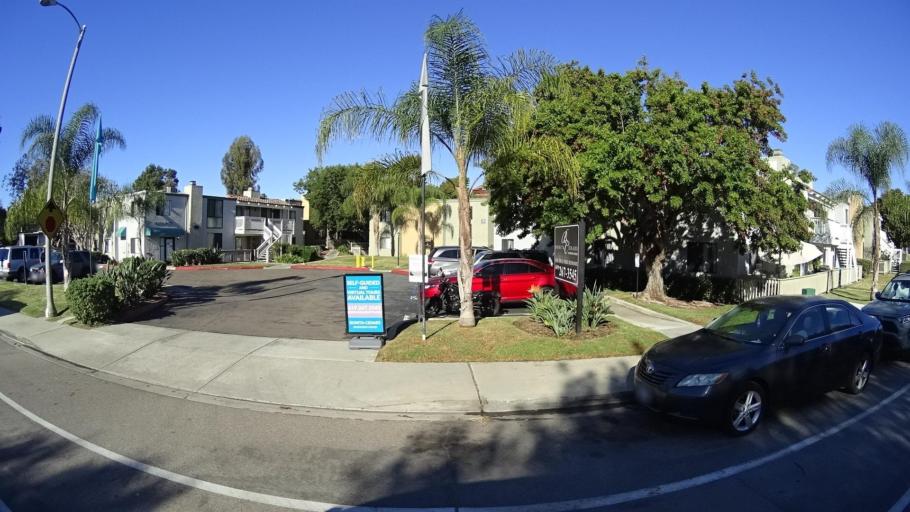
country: US
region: California
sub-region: San Diego County
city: Bonita
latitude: 32.6803
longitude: -117.0268
